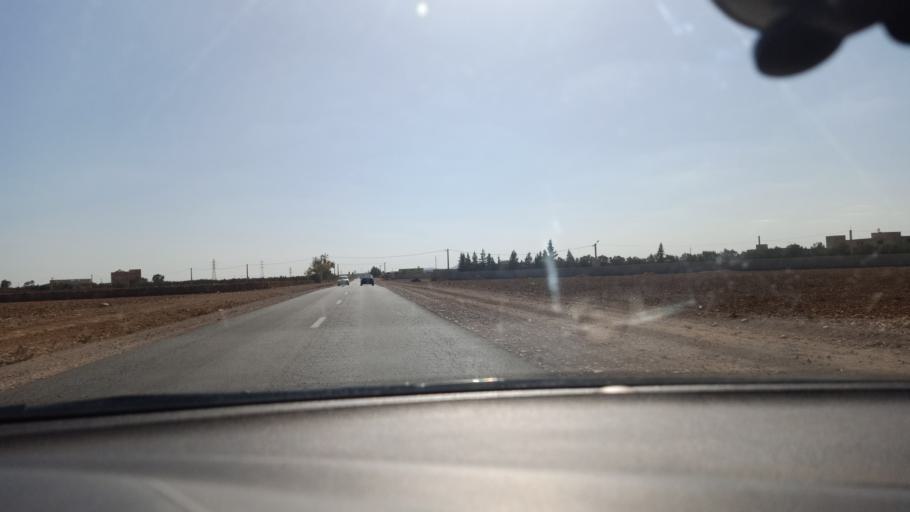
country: MA
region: Doukkala-Abda
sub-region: Safi
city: Youssoufia
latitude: 32.1197
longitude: -8.6044
